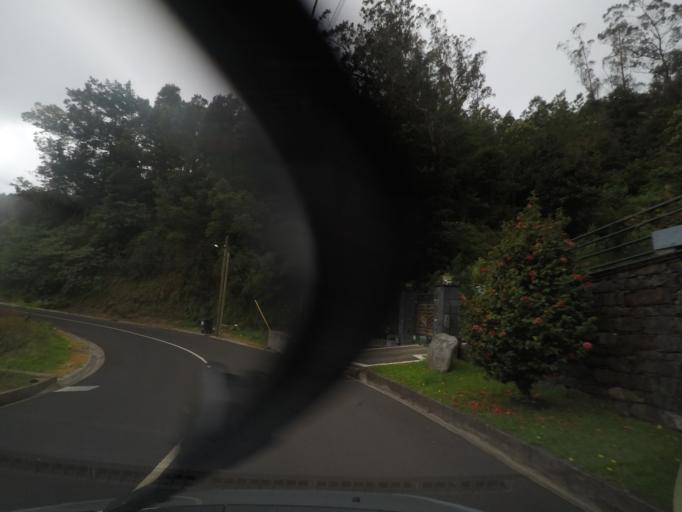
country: PT
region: Madeira
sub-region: Santa Cruz
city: Camacha
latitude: 32.7417
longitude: -16.8339
